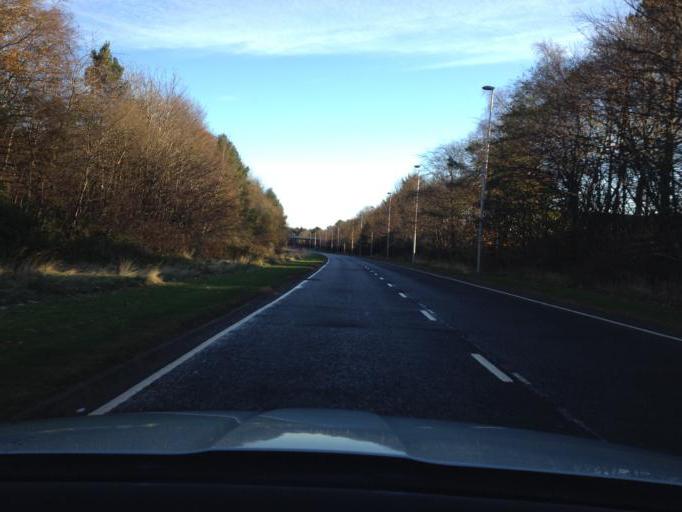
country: GB
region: Scotland
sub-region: West Lothian
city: Livingston
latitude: 55.8884
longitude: -3.5425
